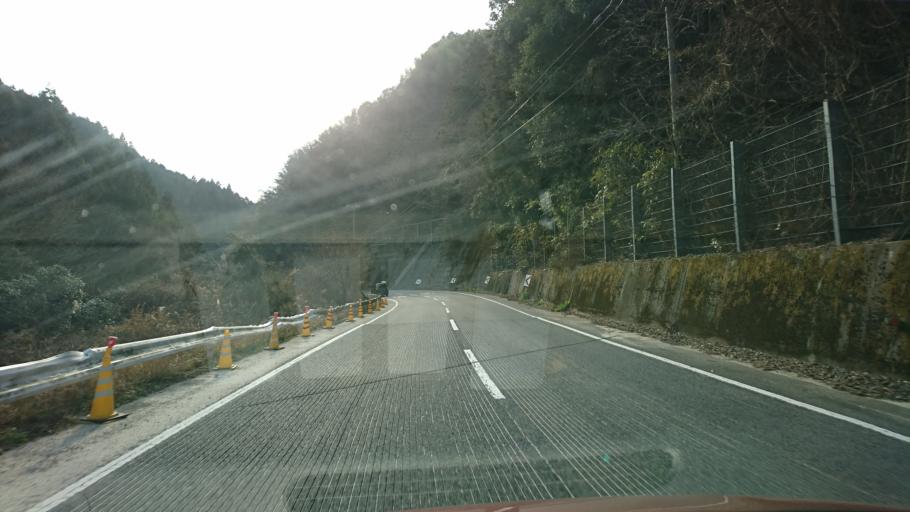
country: JP
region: Ehime
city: Hojo
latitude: 33.9130
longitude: 132.8795
